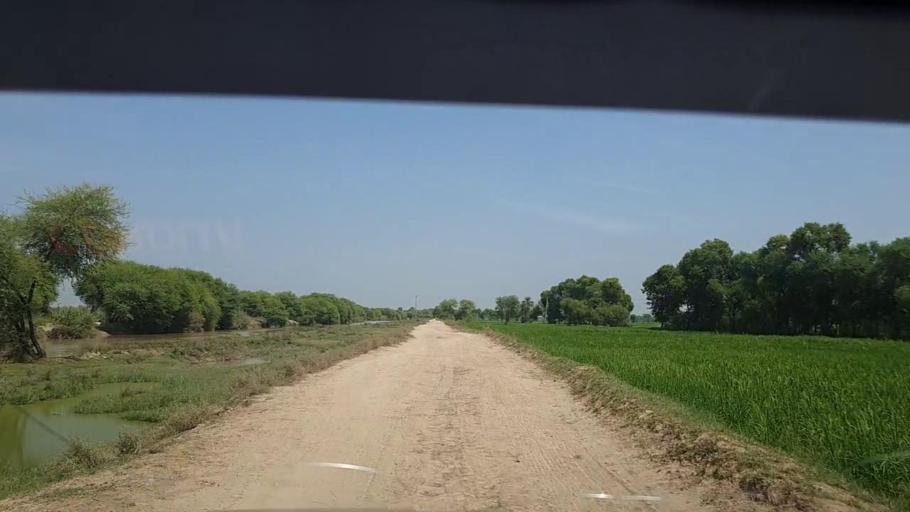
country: PK
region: Sindh
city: Tangwani
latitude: 28.2314
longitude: 68.9389
